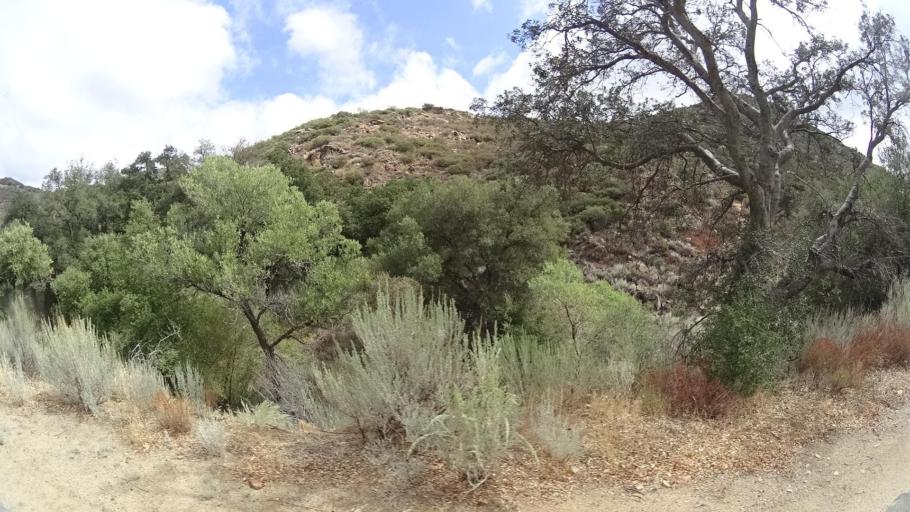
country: US
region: California
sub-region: San Diego County
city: Pine Valley
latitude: 32.7752
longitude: -116.4500
